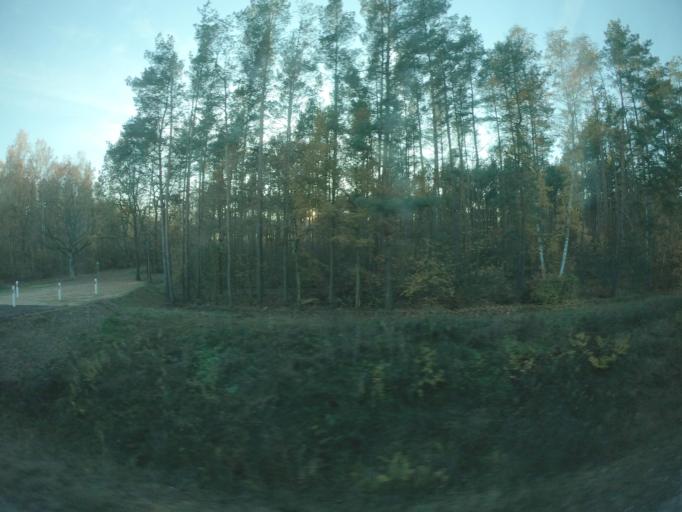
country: PL
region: Lubusz
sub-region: Powiat slubicki
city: Rzepin
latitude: 52.3321
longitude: 14.8372
